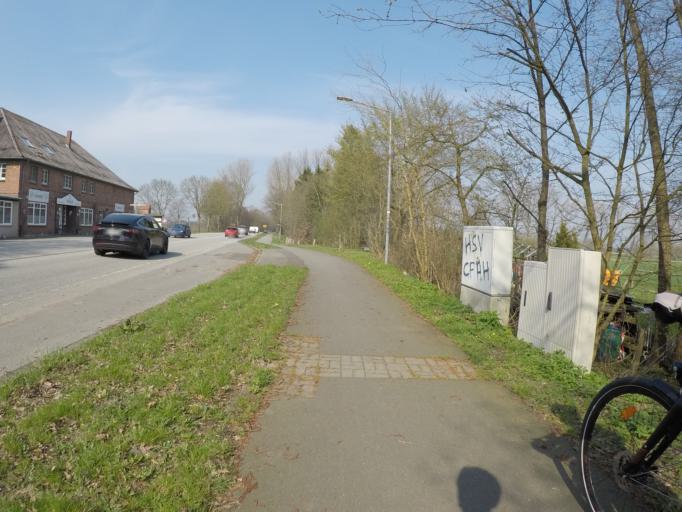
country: DE
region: Schleswig-Holstein
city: Kayhude
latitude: 53.7705
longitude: 10.1242
